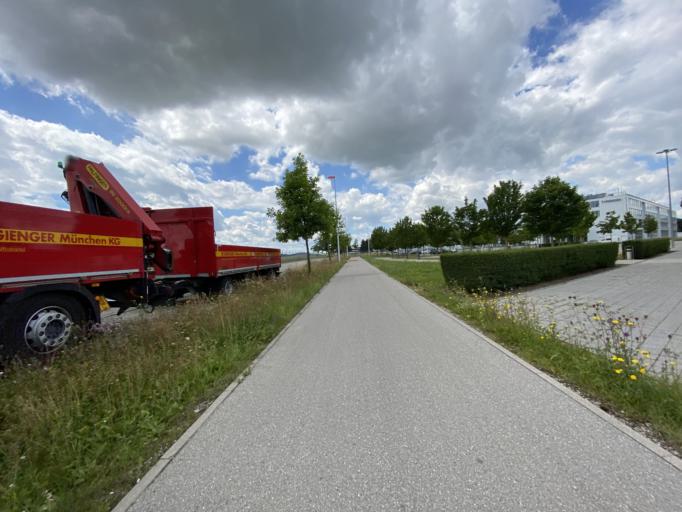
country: DE
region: Bavaria
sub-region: Upper Bavaria
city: Gilching
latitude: 48.0924
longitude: 11.2938
